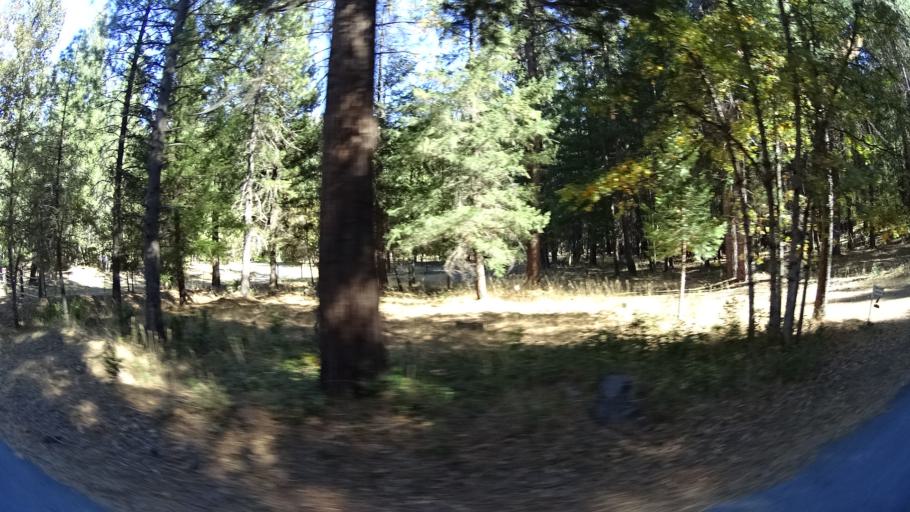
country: US
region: California
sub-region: Siskiyou County
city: Happy Camp
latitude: 41.3211
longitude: -123.0622
